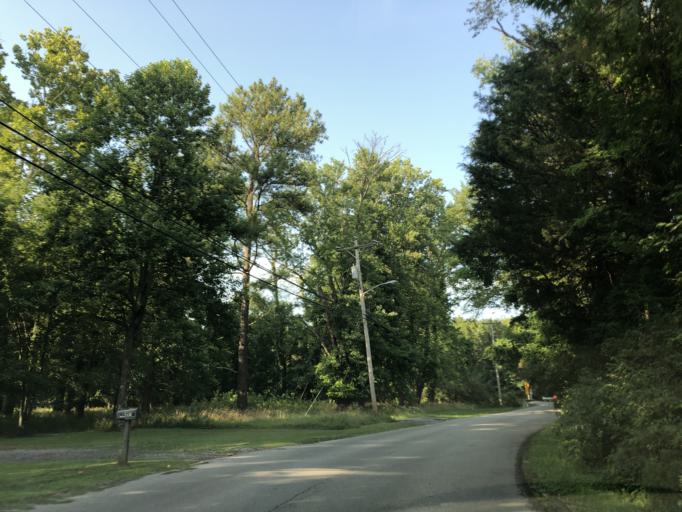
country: US
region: Tennessee
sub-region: Davidson County
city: Lakewood
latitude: 36.1454
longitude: -86.6545
